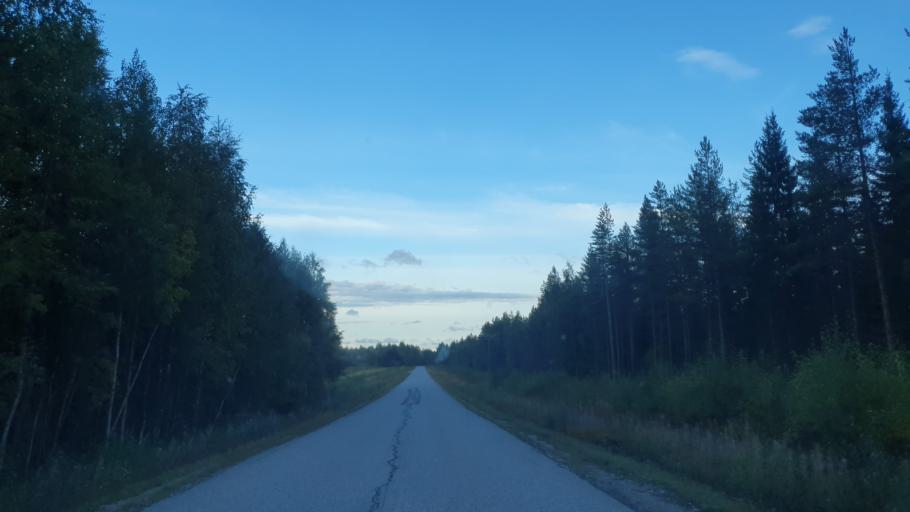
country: FI
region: Kainuu
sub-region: Kehys-Kainuu
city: Kuhmo
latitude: 64.4182
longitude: 29.9119
